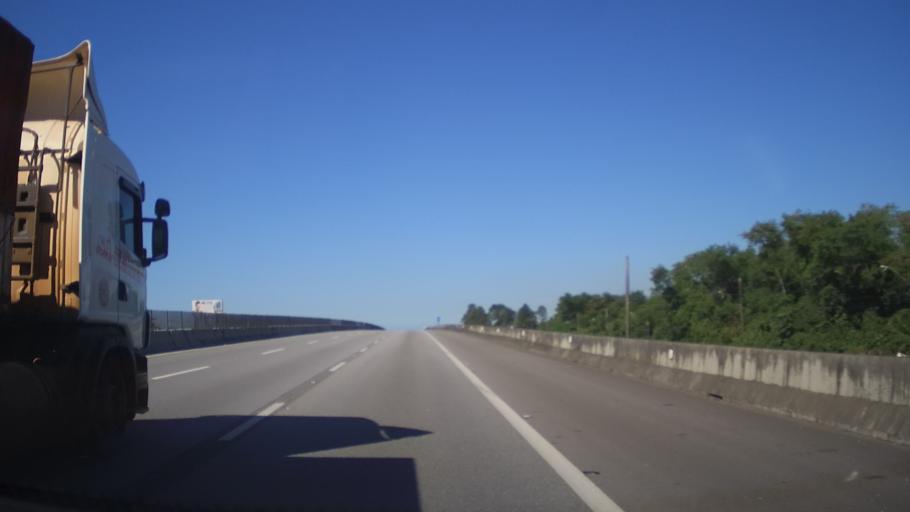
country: BR
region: Sao Paulo
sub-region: Cubatao
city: Cubatao
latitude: -23.9529
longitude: -46.4658
